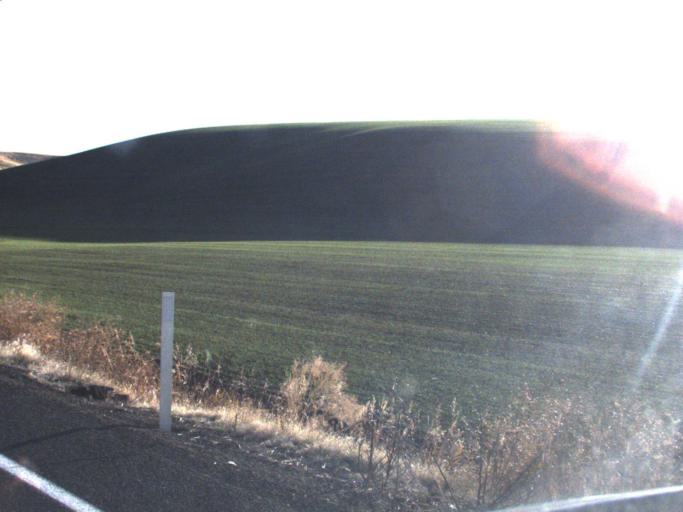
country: US
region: Washington
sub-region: Walla Walla County
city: Waitsburg
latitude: 46.1956
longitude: -118.1382
